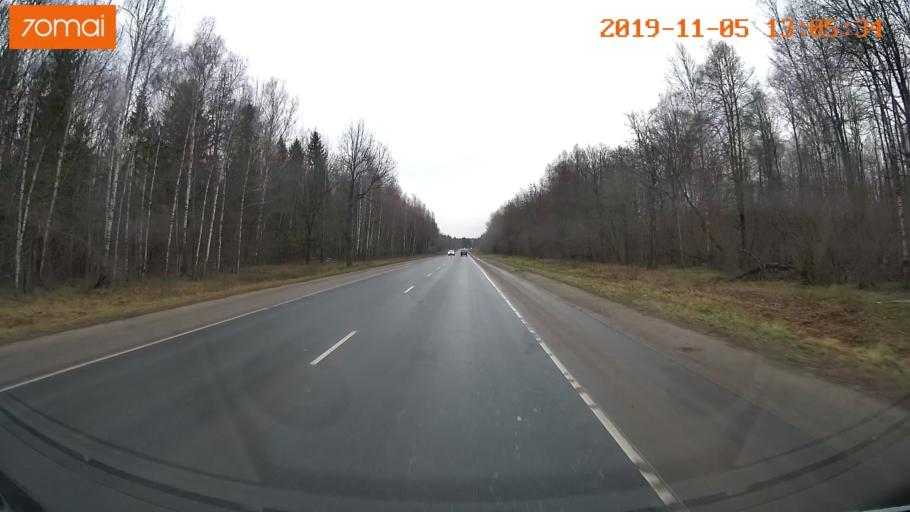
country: RU
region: Ivanovo
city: Kitovo
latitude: 56.8817
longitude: 41.2456
